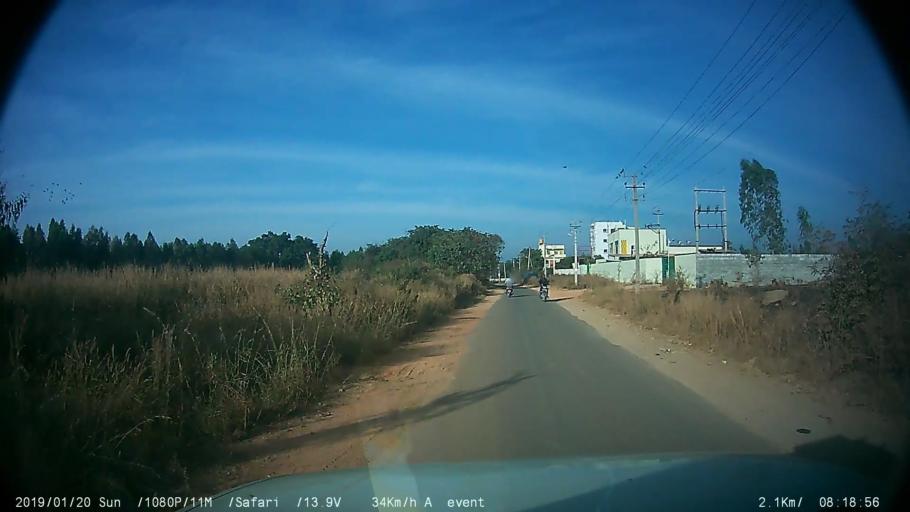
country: IN
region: Karnataka
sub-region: Bangalore Urban
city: Anekal
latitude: 12.8196
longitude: 77.6448
